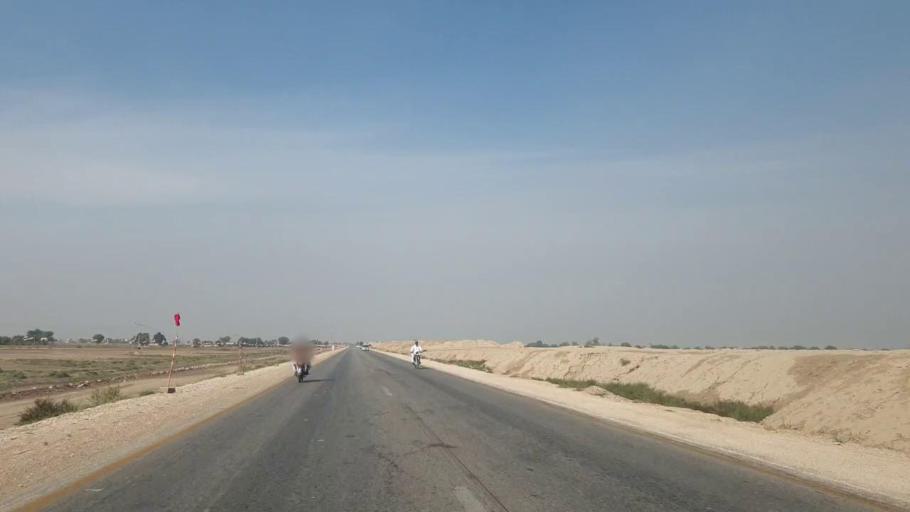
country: PK
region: Sindh
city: Sann
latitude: 25.9666
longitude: 68.1899
